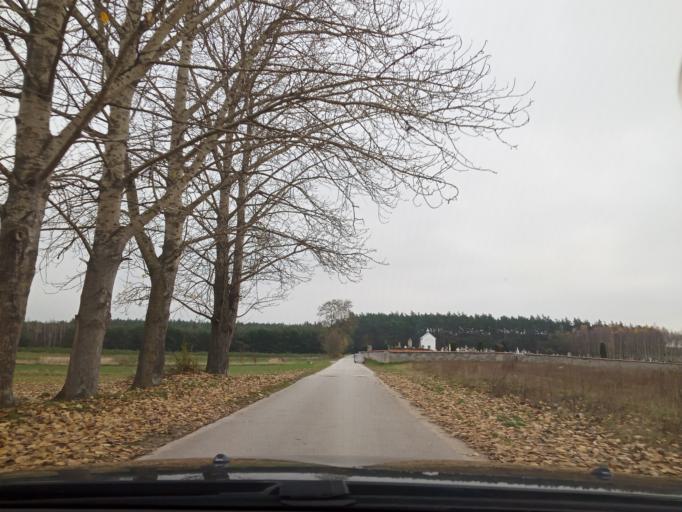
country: PL
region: Swietokrzyskie
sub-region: Powiat jedrzejowski
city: Imielno
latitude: 50.5829
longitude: 20.4512
